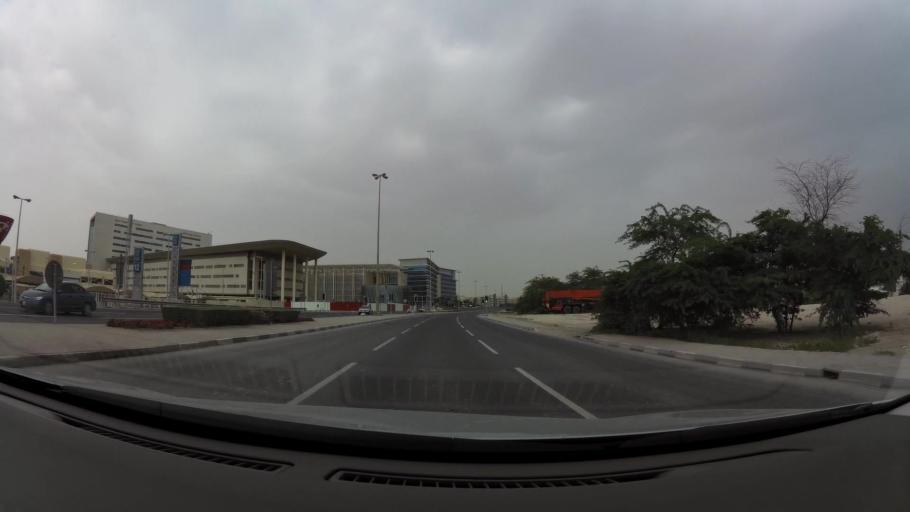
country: QA
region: Baladiyat ad Dawhah
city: Doha
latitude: 25.2945
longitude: 51.5124
